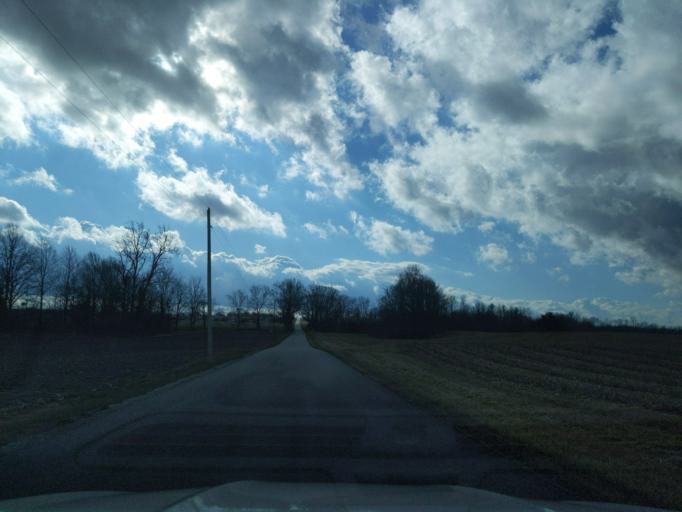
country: US
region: Indiana
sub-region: Decatur County
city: Greensburg
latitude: 39.3726
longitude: -85.4986
